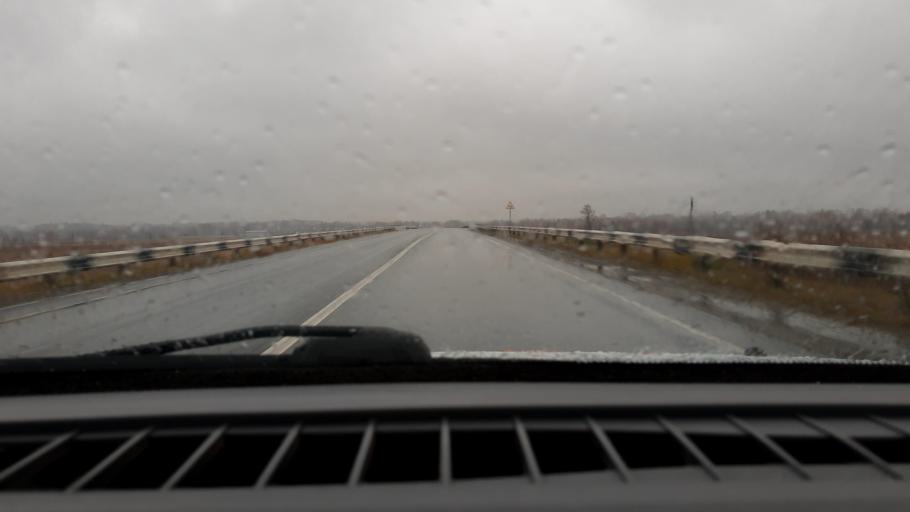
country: RU
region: Nizjnij Novgorod
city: Sitniki
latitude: 56.4932
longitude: 44.0233
